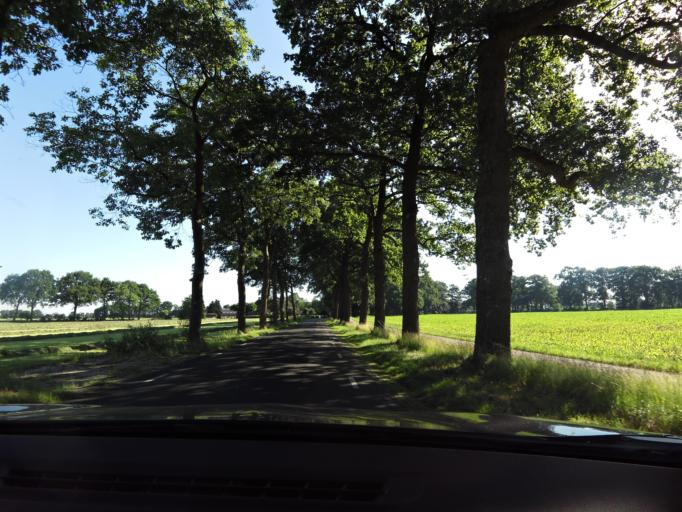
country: NL
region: Gelderland
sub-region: Gemeente Lochem
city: Harfsen
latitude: 52.2857
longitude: 6.3018
